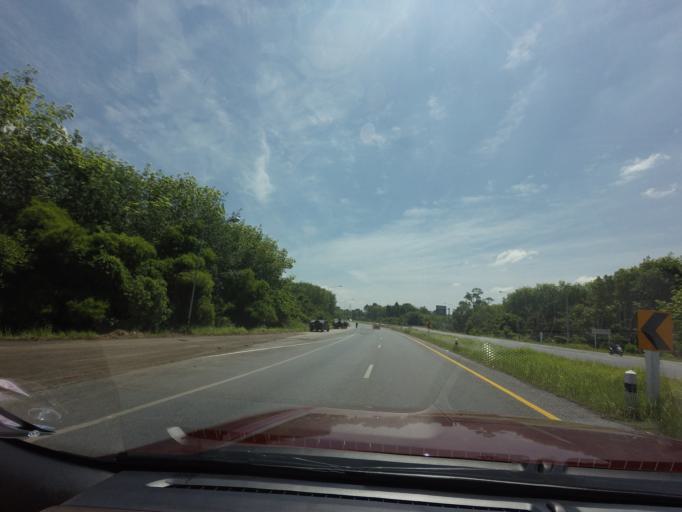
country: TH
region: Yala
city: Yala
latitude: 6.5871
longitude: 101.2609
